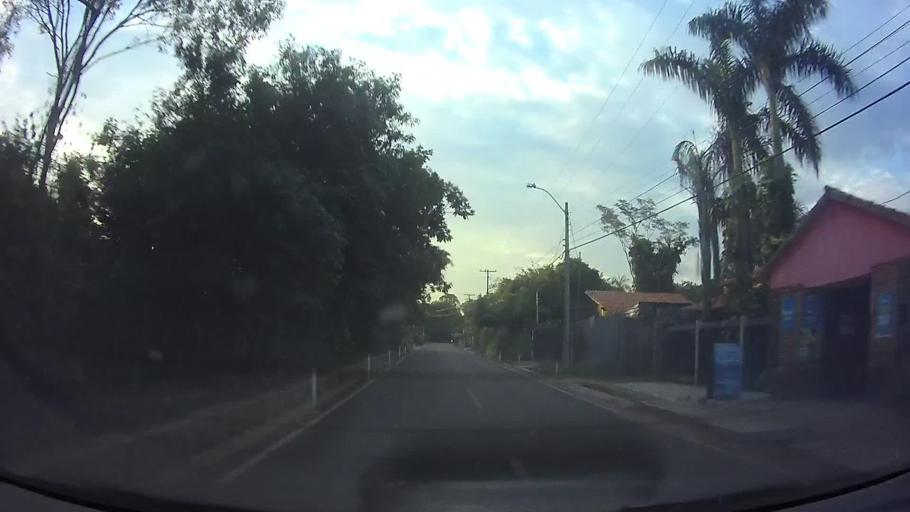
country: PY
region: Central
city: Limpio
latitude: -25.2511
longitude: -57.4975
